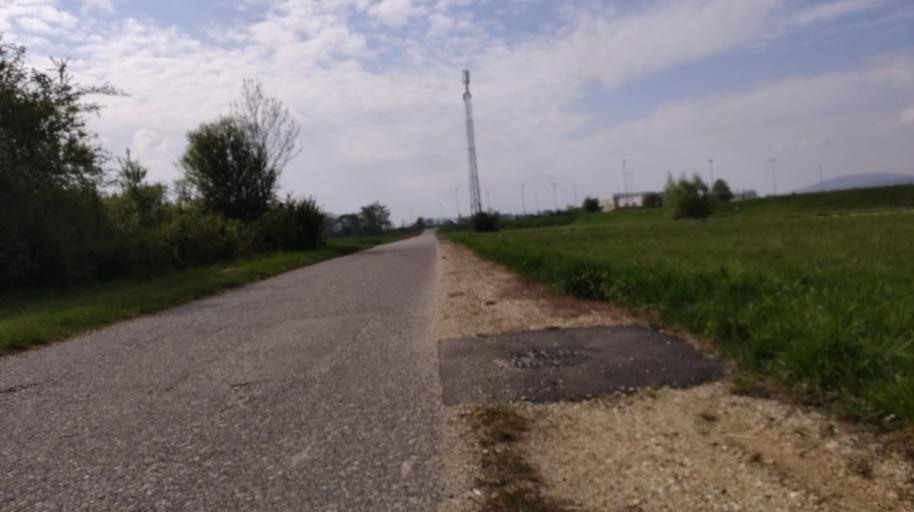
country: AT
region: Burgenland
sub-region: Politischer Bezirk Neusiedl am See
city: Kittsee
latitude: 48.1206
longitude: 17.0593
